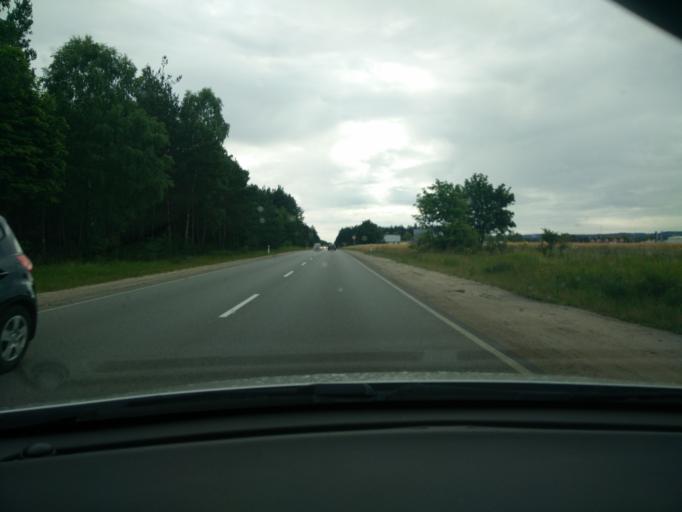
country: PL
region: Pomeranian Voivodeship
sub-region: Powiat pucki
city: Kosakowo
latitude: 54.6046
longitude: 18.4597
